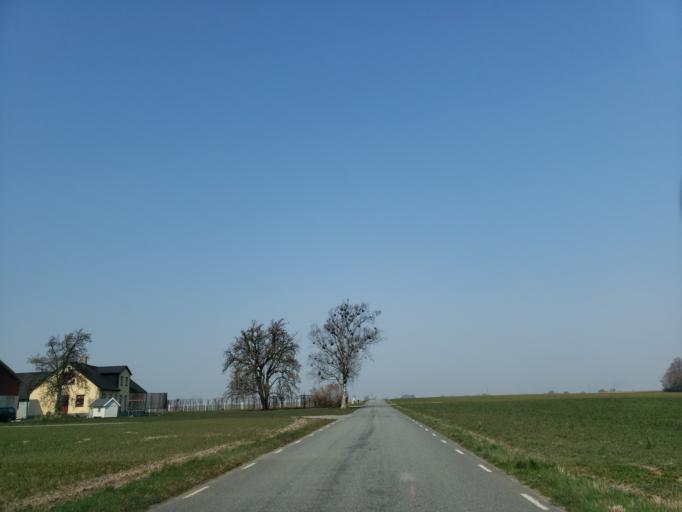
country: SE
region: Skane
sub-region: Simrishamns Kommun
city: Simrishamn
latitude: 55.4572
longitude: 14.2133
